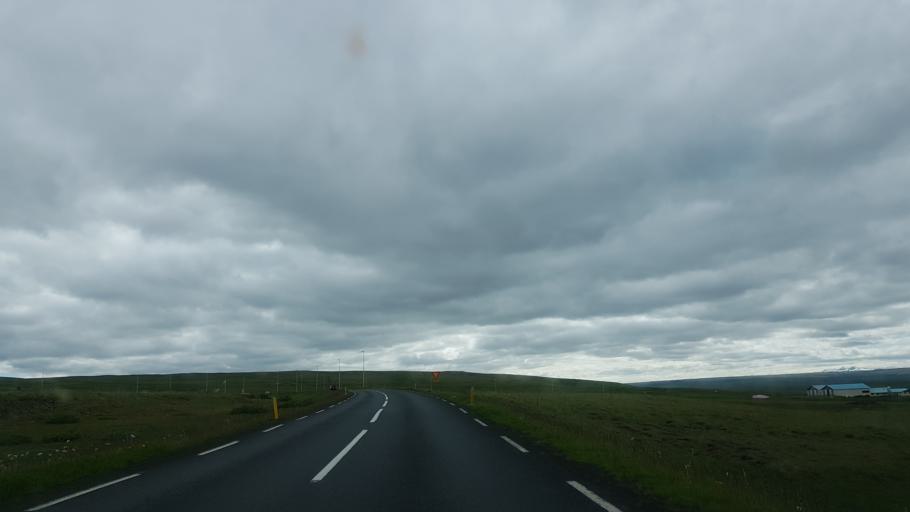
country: IS
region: Northwest
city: Saudarkrokur
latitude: 65.3557
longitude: -20.8883
